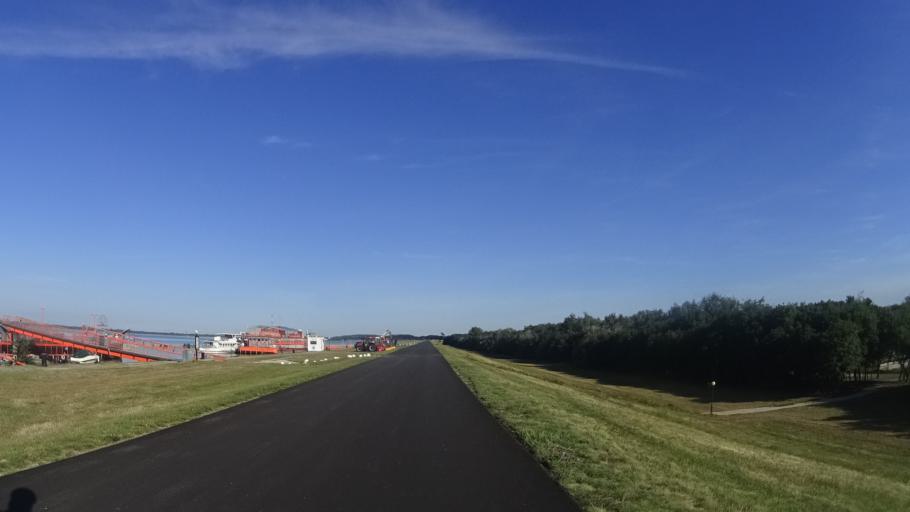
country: SK
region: Trnavsky
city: Samorin
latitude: 48.0082
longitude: 17.3060
